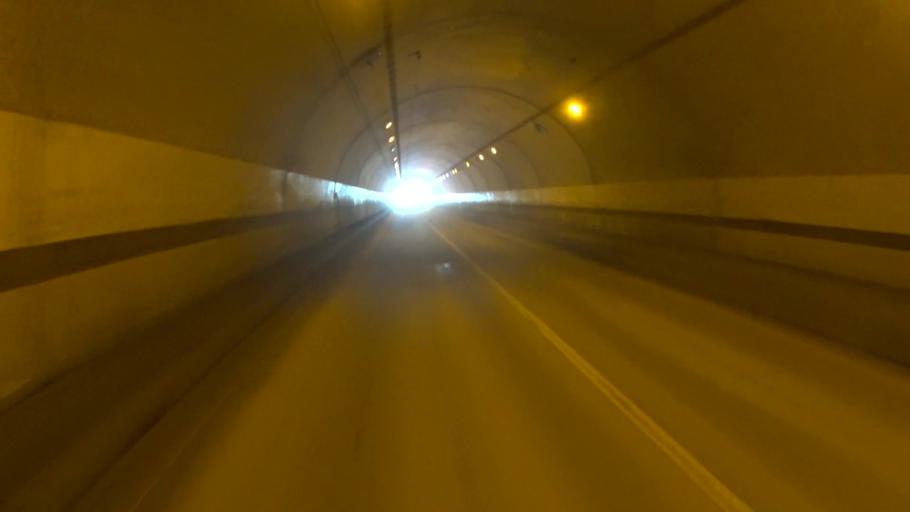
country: JP
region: Kyoto
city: Miyazu
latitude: 35.6622
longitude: 135.2595
